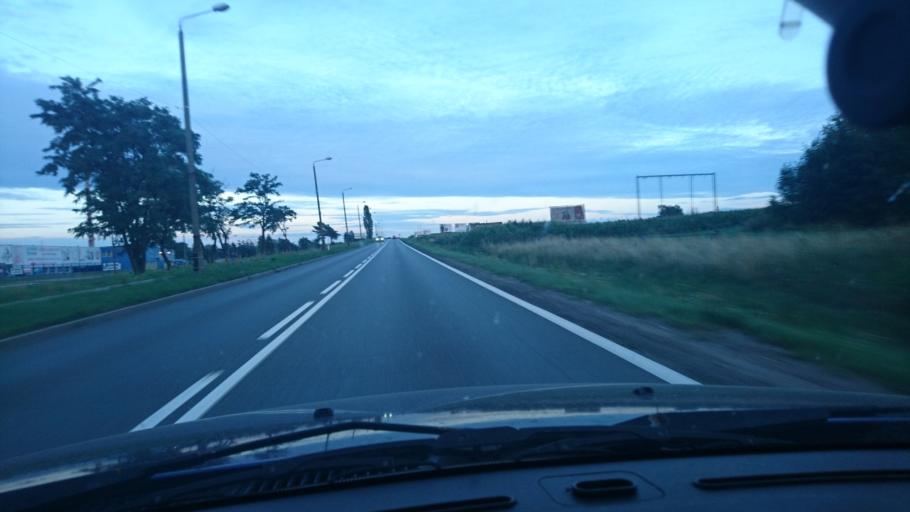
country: PL
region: Silesian Voivodeship
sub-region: Powiat tarnogorski
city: Tarnowskie Gory
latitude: 50.4626
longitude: 18.8213
